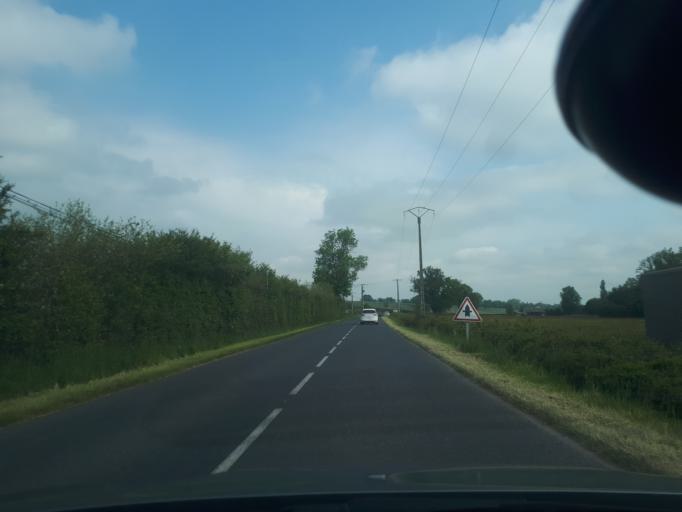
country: FR
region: Auvergne
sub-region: Departement de l'Allier
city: Saint-Gerand-le-Puy
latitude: 46.3508
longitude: 3.5792
